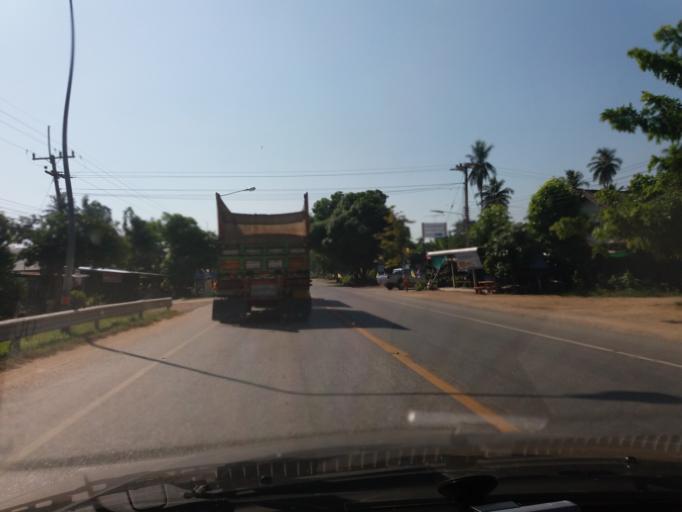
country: TH
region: Kamphaeng Phet
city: Khanu Woralaksaburi
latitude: 16.1110
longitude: 99.8354
